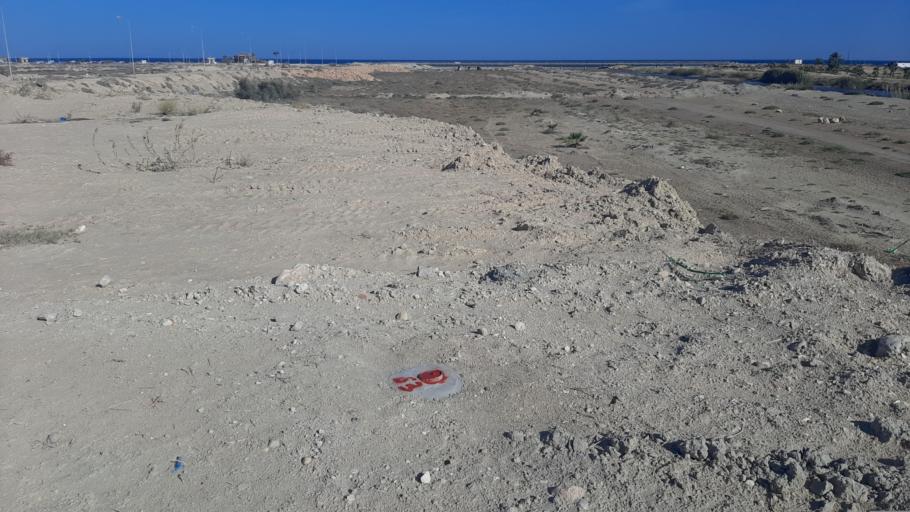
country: TN
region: Qabis
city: Gabes
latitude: 33.8814
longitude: 10.1159
